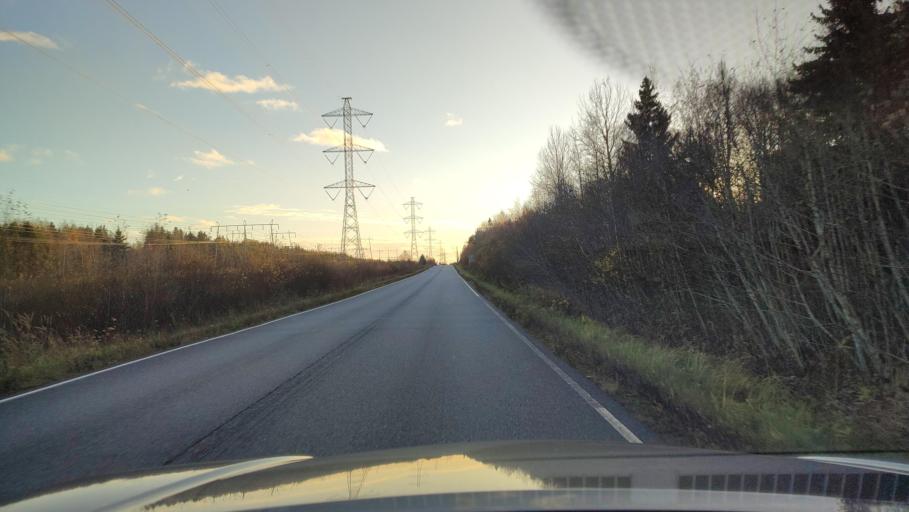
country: FI
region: Ostrobothnia
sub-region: Sydosterbotten
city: Kristinestad
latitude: 62.2931
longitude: 21.3671
